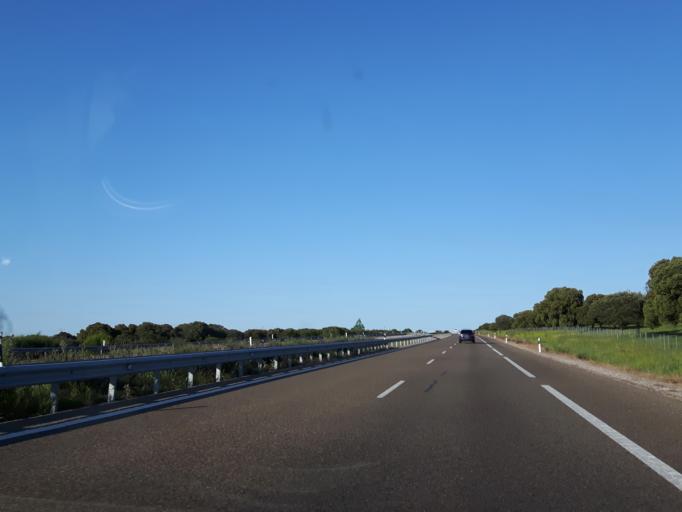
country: ES
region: Castille and Leon
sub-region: Provincia de Salamanca
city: Aldehuela de la Boveda
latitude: 40.8565
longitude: -6.0337
